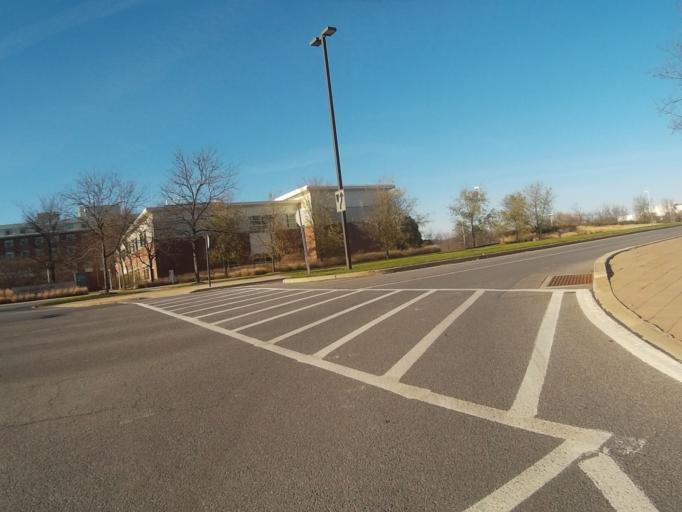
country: US
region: Pennsylvania
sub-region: Centre County
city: Houserville
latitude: 40.8309
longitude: -77.8438
